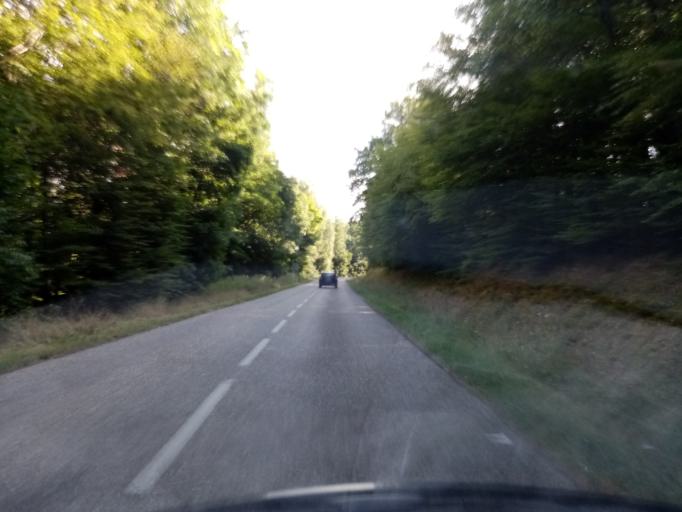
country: FR
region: Alsace
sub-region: Departement du Bas-Rhin
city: Ville
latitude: 48.3407
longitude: 7.3648
